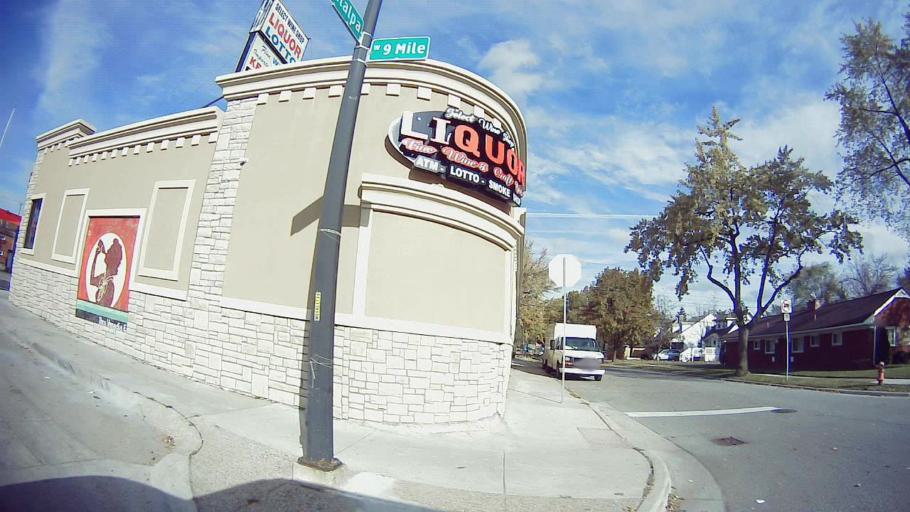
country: US
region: Michigan
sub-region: Oakland County
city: Pleasant Ridge
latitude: 42.4602
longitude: -83.1522
